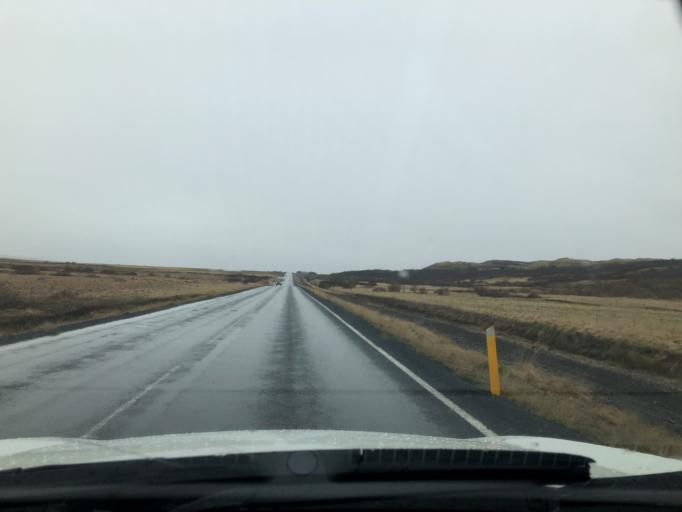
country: IS
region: South
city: Selfoss
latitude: 64.2941
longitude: -20.3351
